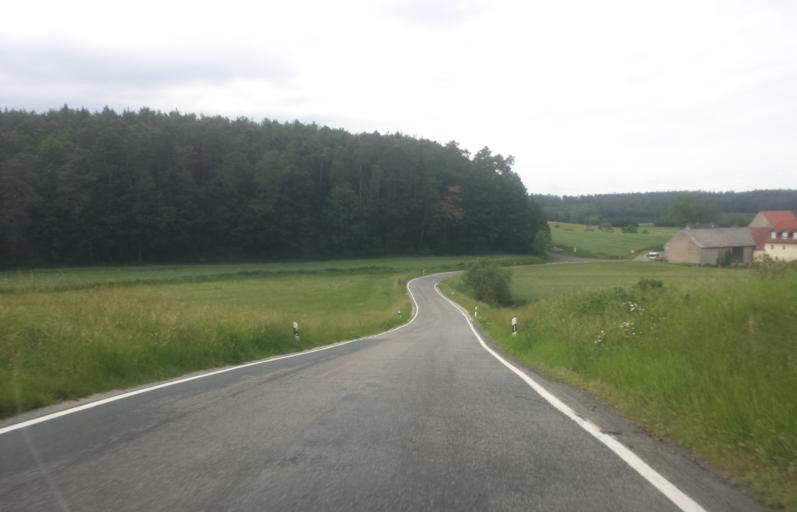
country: DE
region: Bavaria
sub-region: Upper Franconia
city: Schlusselfeld
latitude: 49.7807
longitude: 10.6526
